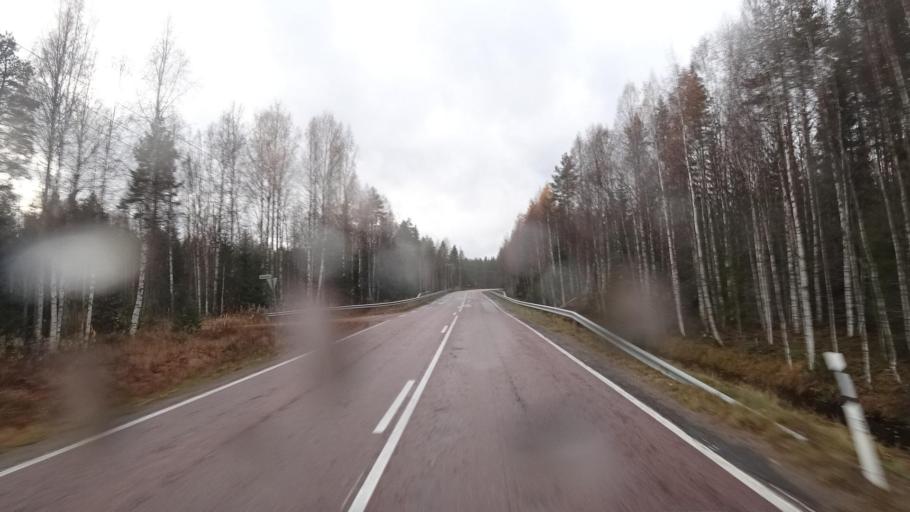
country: FI
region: Southern Savonia
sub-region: Mikkeli
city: Kangasniemi
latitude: 62.0743
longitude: 26.6865
